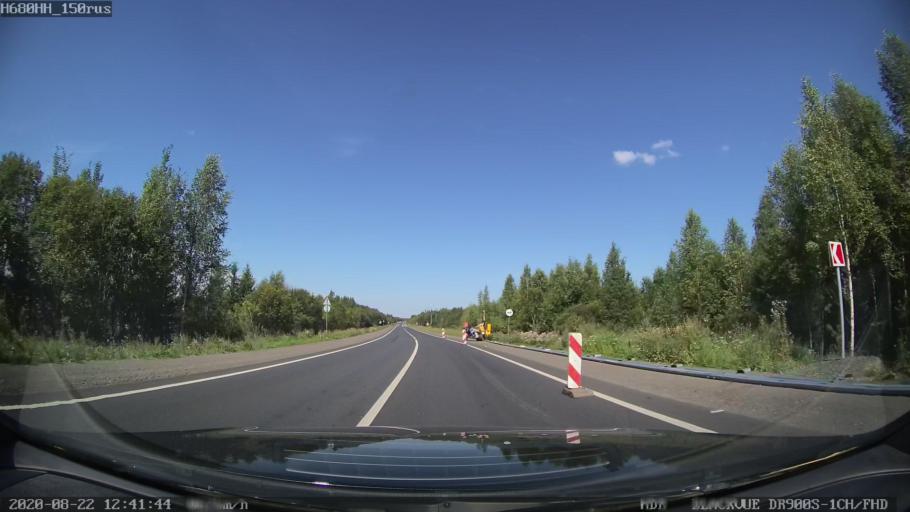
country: RU
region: Tverskaya
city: Rameshki
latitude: 57.3518
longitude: 36.0997
